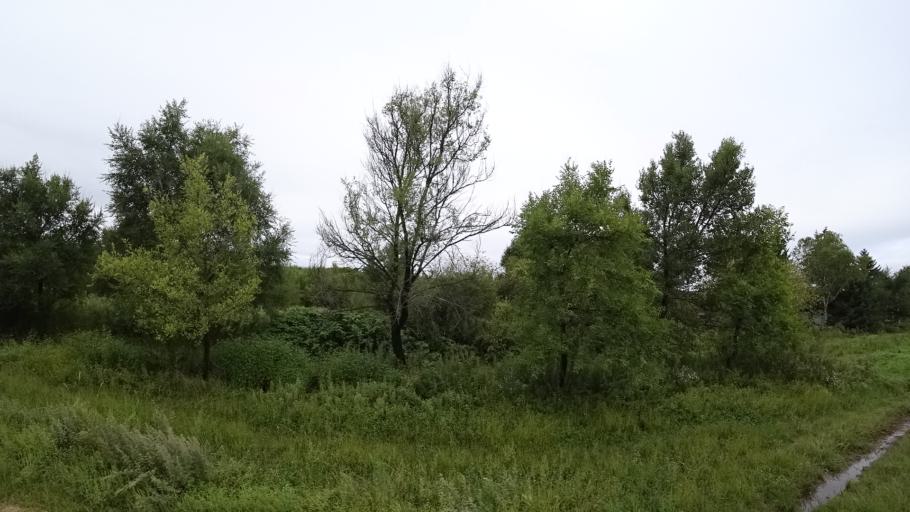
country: RU
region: Primorskiy
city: Rettikhovka
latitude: 44.0568
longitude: 132.6552
